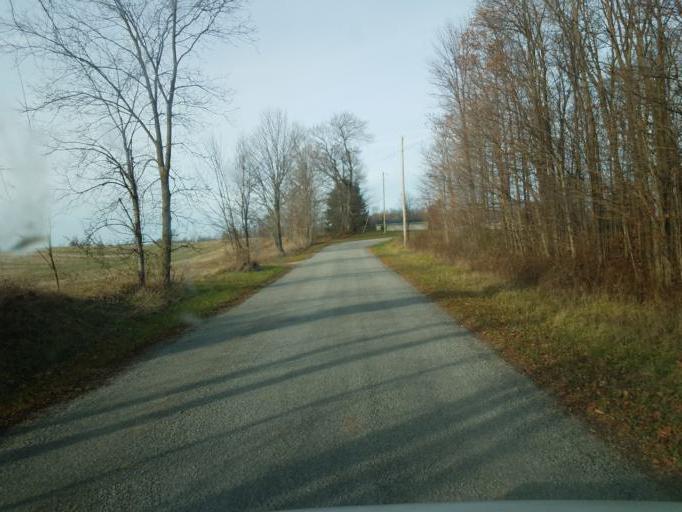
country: US
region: Ohio
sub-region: Morrow County
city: Mount Gilead
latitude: 40.5720
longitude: -82.7098
